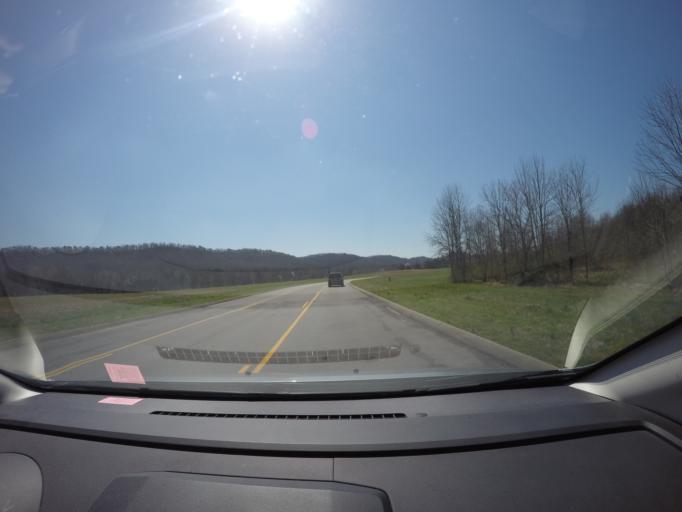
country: US
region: Tennessee
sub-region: Hamilton County
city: Collegedale
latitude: 35.0591
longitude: -85.0716
